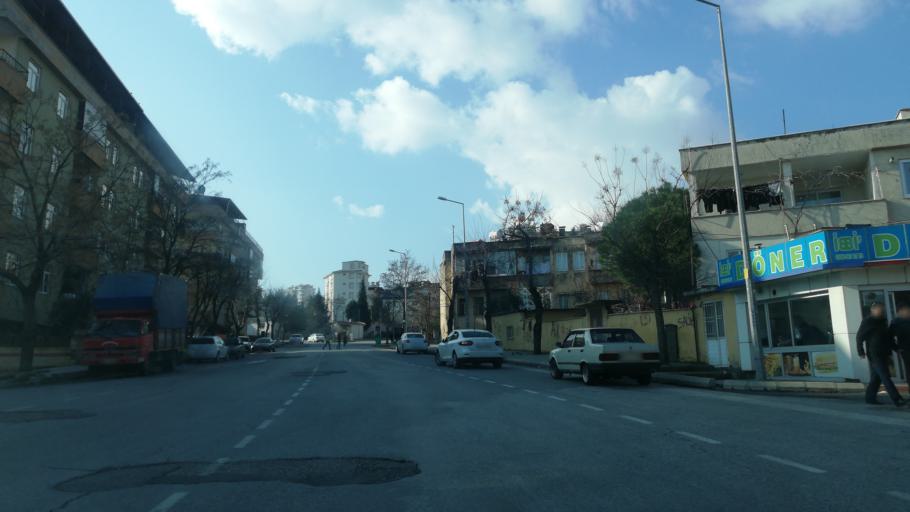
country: TR
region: Kahramanmaras
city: Kahramanmaras
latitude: 37.5888
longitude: 36.9081
